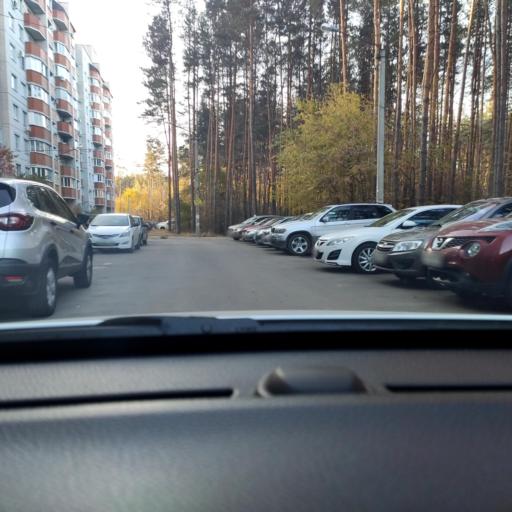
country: RU
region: Voronezj
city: Voronezh
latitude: 51.6888
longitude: 39.2780
